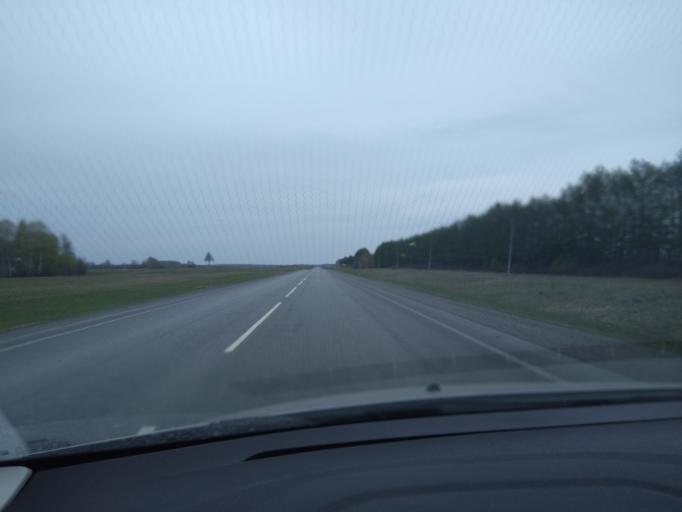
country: RU
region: Sverdlovsk
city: Talitsa
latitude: 57.0690
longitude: 63.5805
